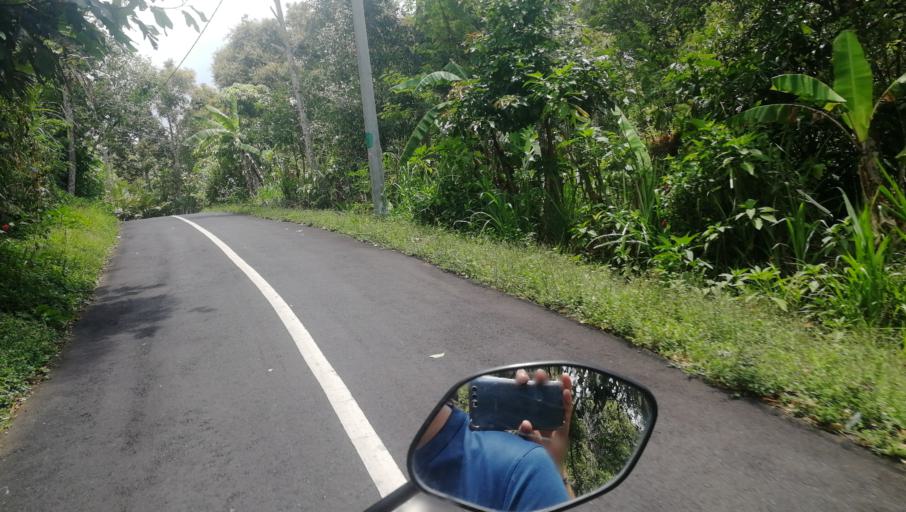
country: ID
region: Bali
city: Munduk
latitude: -8.2965
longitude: 115.0500
